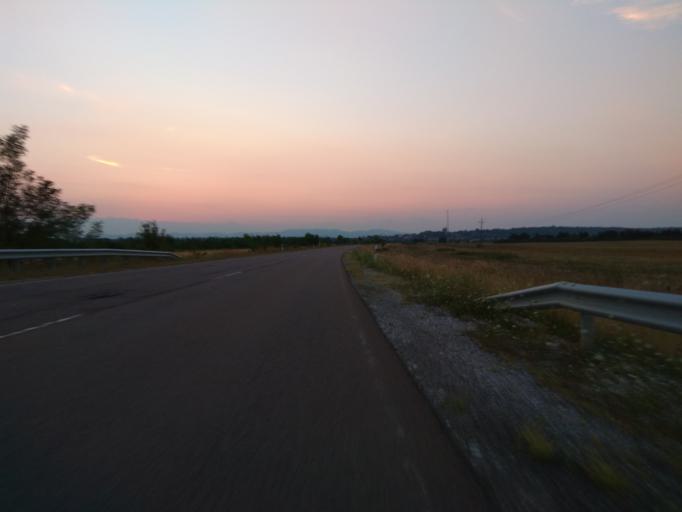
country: HU
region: Borsod-Abauj-Zemplen
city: Emod
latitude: 47.9261
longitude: 20.8356
